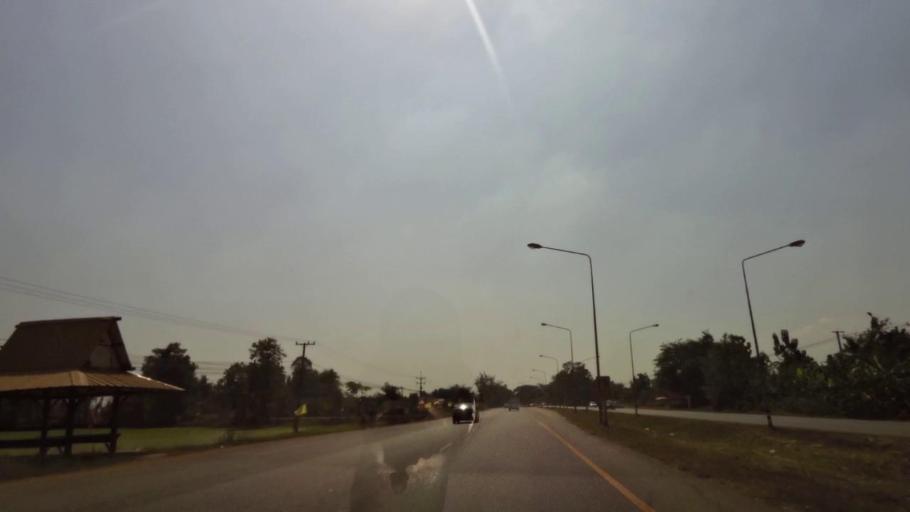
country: TH
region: Phichit
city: Wachira Barami
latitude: 16.3733
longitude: 100.1335
